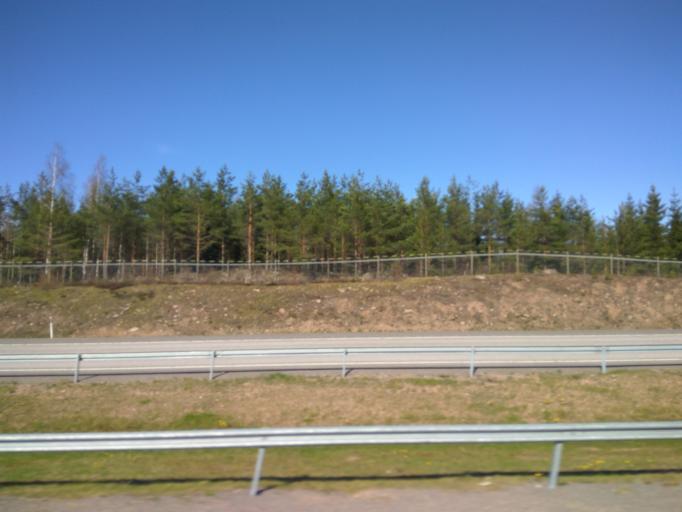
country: FI
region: Uusimaa
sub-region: Loviisa
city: Perna
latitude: 60.4741
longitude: 26.1154
